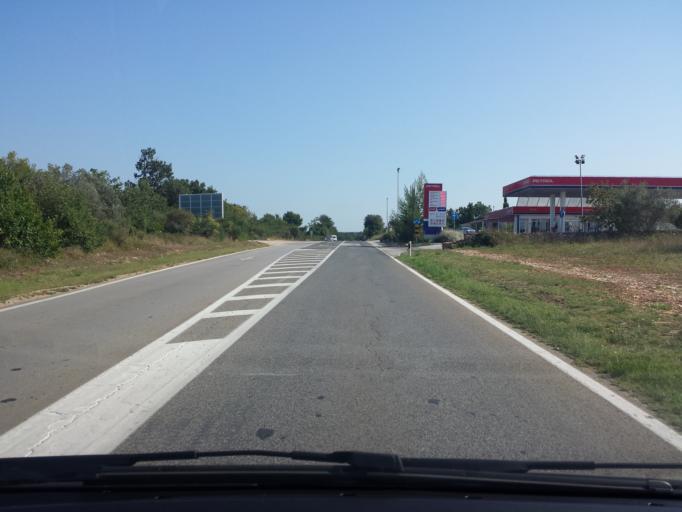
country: HR
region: Istarska
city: Galizana
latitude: 44.9146
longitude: 13.8495
